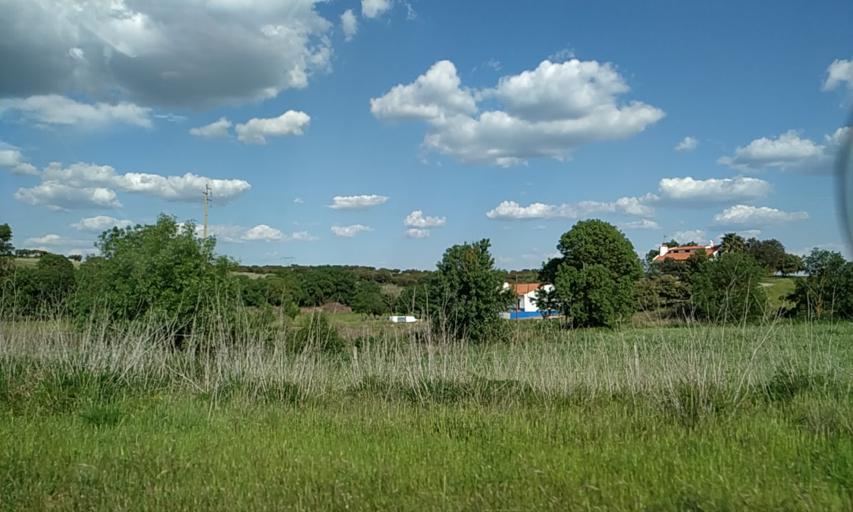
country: PT
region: Evora
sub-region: Estremoz
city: Estremoz
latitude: 38.8772
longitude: -7.5623
